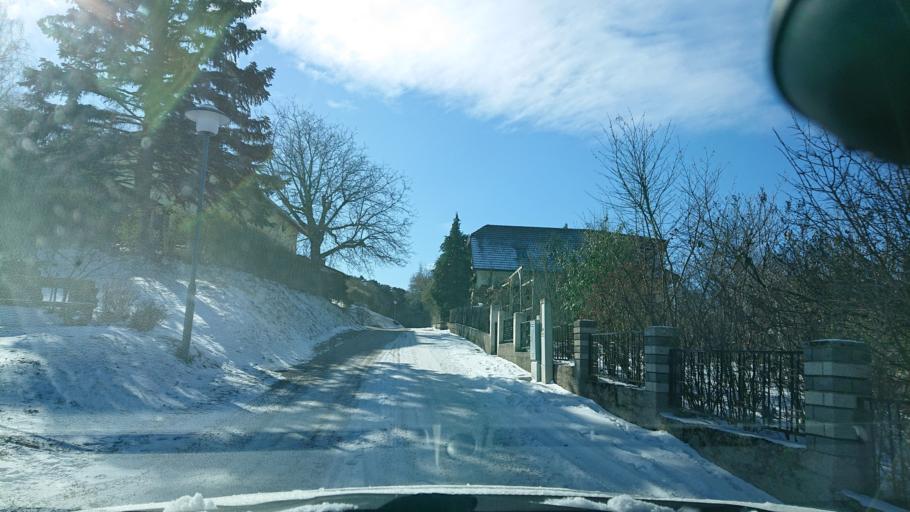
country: AT
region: Lower Austria
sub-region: Politischer Bezirk Baden
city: Hernstein
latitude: 47.8865
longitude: 16.0960
